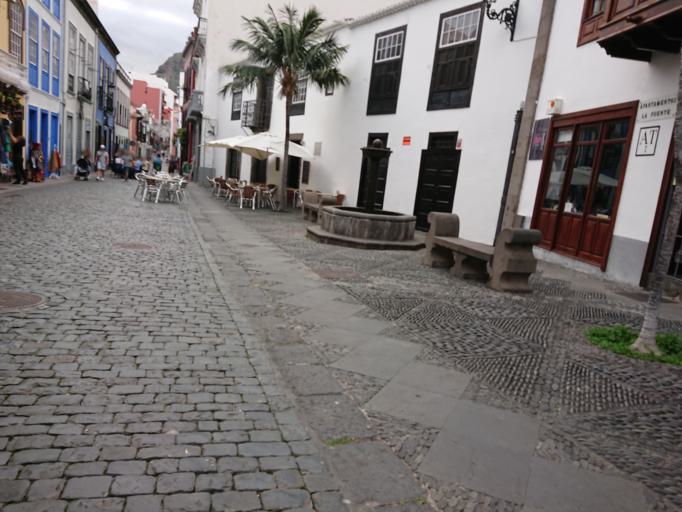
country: ES
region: Canary Islands
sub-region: Provincia de Santa Cruz de Tenerife
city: Santa Cruz de la Palma
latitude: 28.6857
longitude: -17.7626
